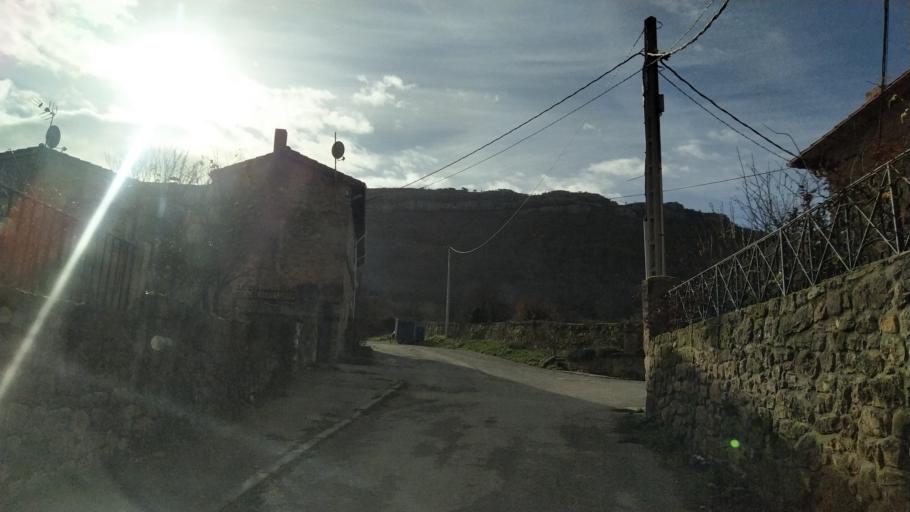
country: ES
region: Cantabria
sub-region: Provincia de Cantabria
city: San Martin de Elines
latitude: 42.8313
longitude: -3.8608
